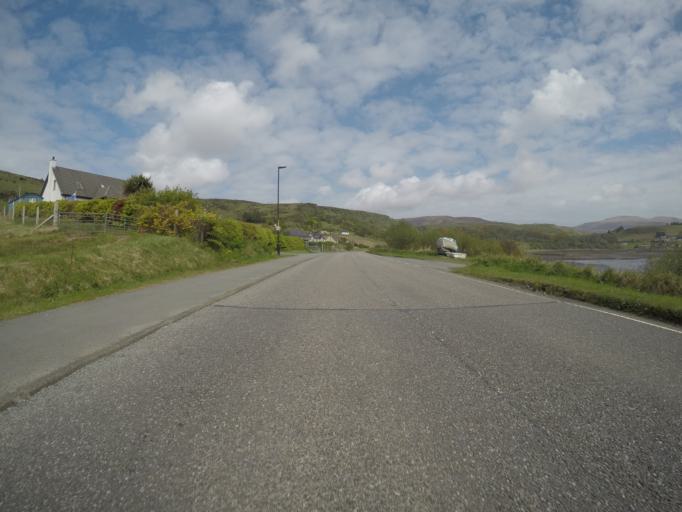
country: GB
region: Scotland
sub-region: Highland
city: Portree
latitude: 57.5890
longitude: -6.3743
